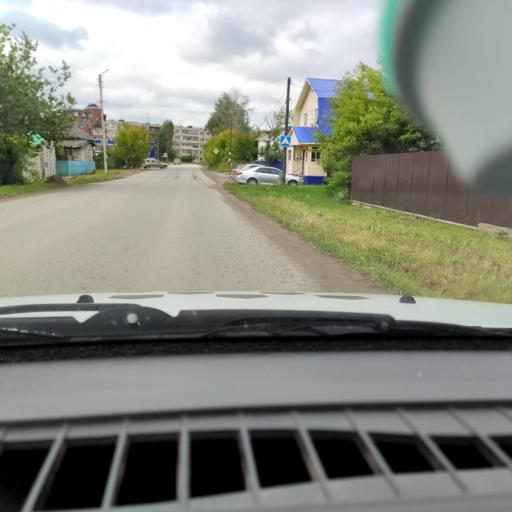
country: RU
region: Perm
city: Dobryanka
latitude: 58.4681
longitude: 56.4107
